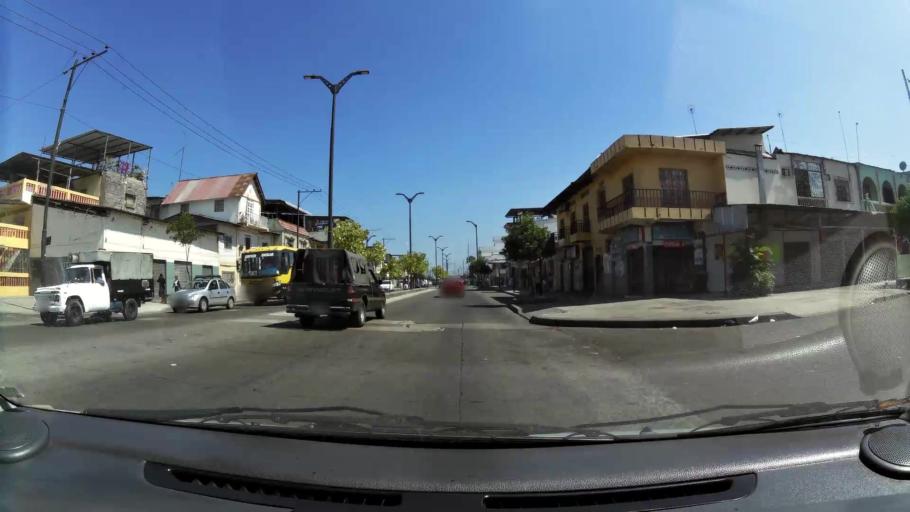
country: EC
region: Guayas
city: Guayaquil
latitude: -2.2144
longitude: -79.9344
